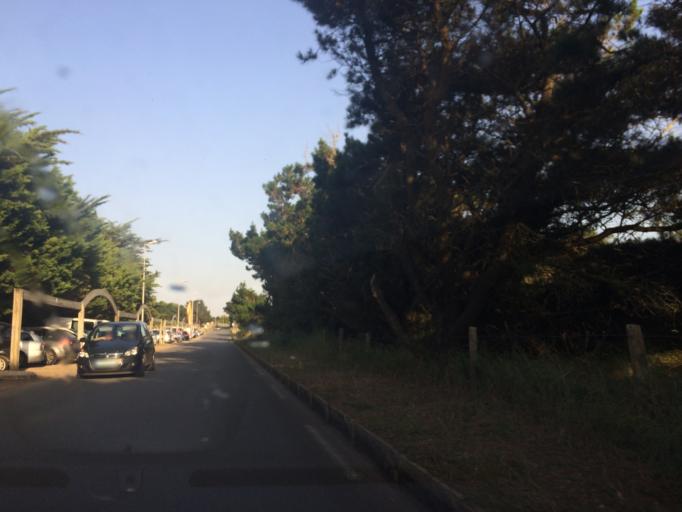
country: FR
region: Brittany
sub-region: Departement du Morbihan
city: Damgan
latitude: 47.5159
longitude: -2.5655
